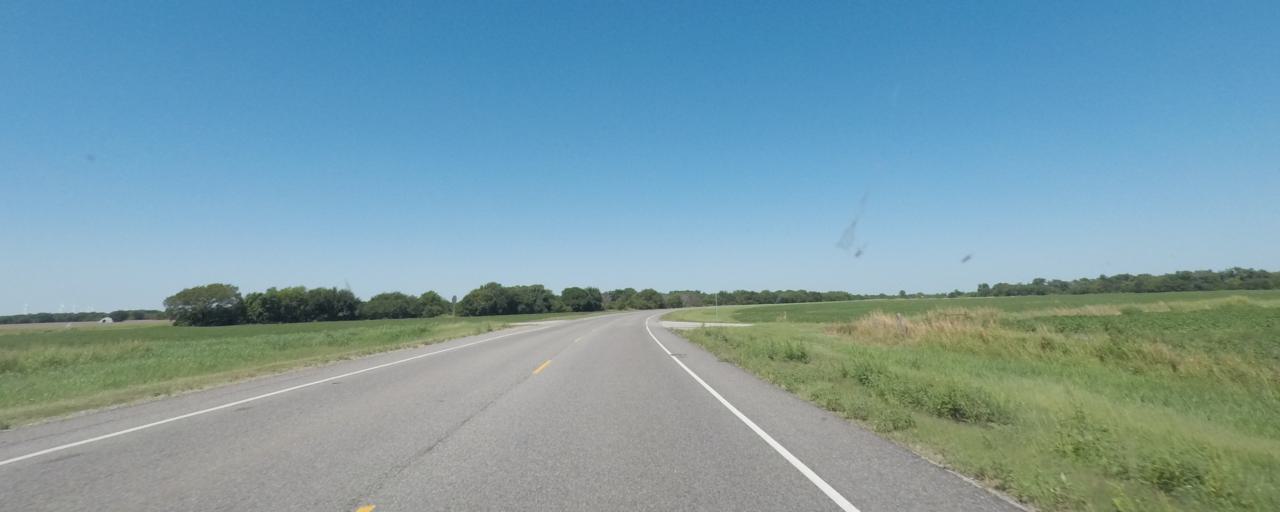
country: US
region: Oklahoma
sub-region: Kay County
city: Blackwell
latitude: 36.9419
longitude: -97.3538
